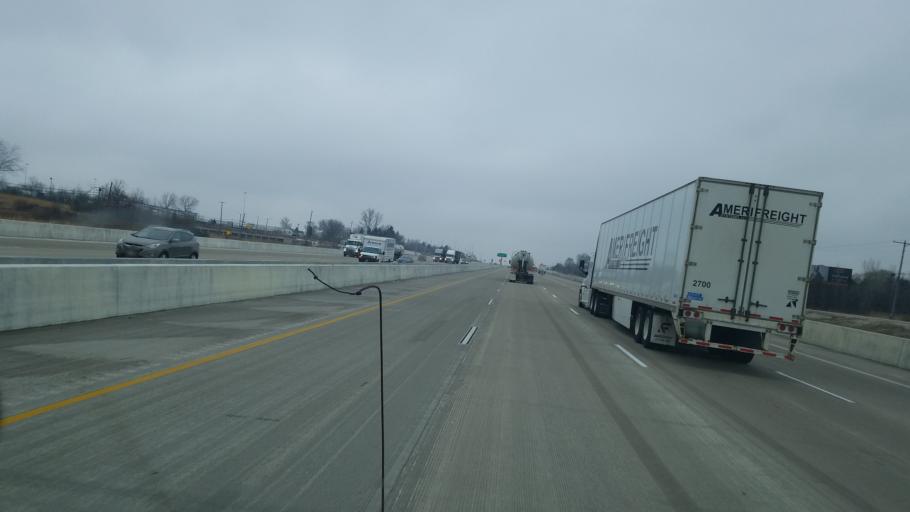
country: US
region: Wisconsin
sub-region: Racine County
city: Caledonia
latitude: 42.7888
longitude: -87.9533
